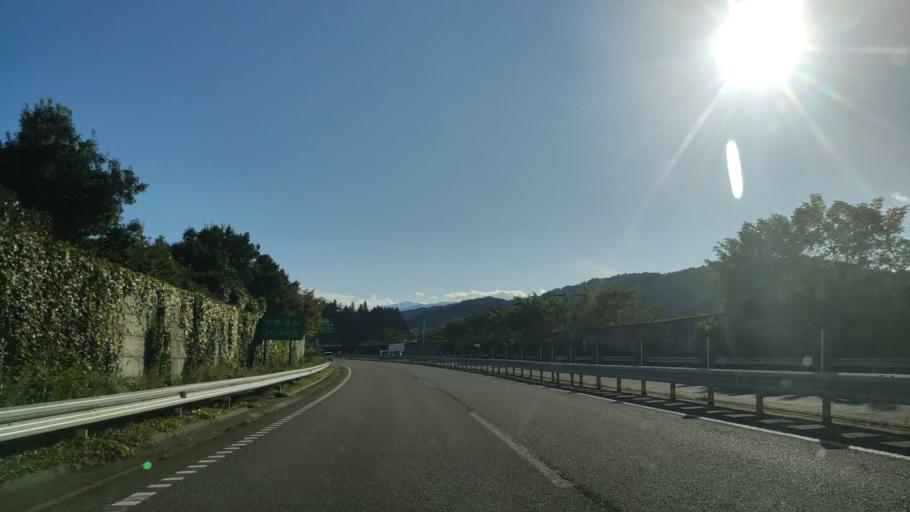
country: JP
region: Nagano
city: Iida
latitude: 35.4797
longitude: 137.7625
